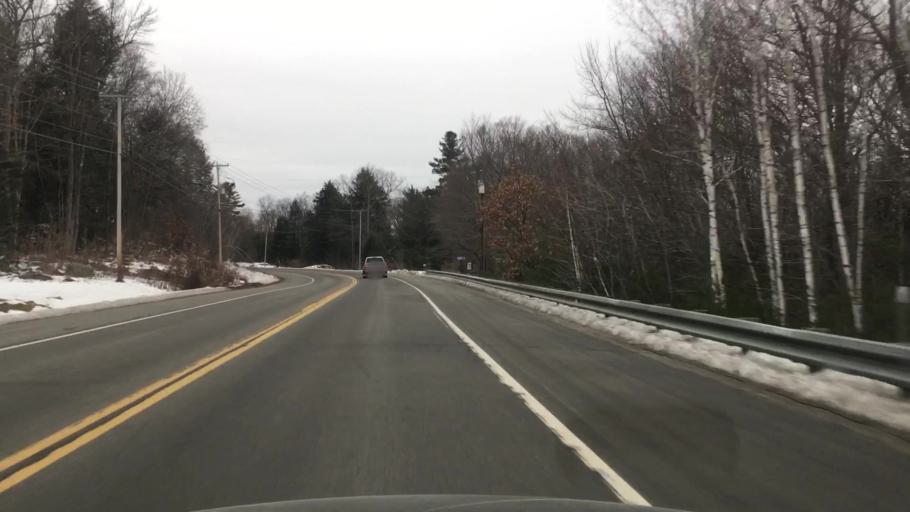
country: US
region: New Hampshire
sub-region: Merrimack County
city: Sutton
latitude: 43.2807
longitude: -71.9749
